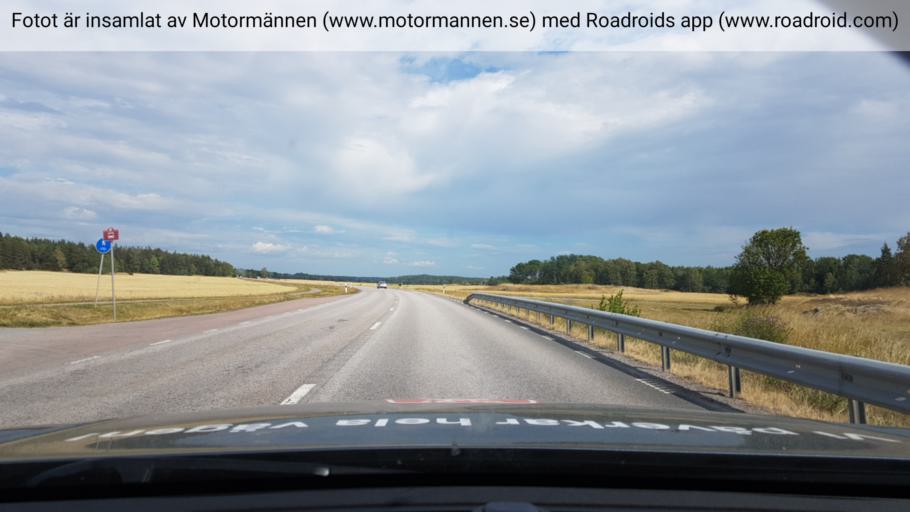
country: SE
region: Uppsala
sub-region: Uppsala Kommun
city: Uppsala
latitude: 59.8513
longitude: 17.4534
